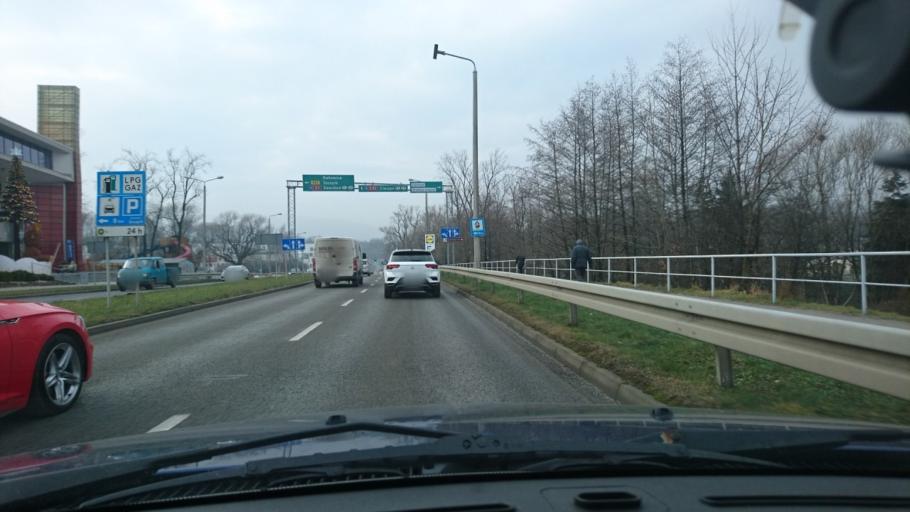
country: PL
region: Silesian Voivodeship
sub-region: Bielsko-Biala
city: Bielsko-Biala
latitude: 49.8039
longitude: 19.0495
